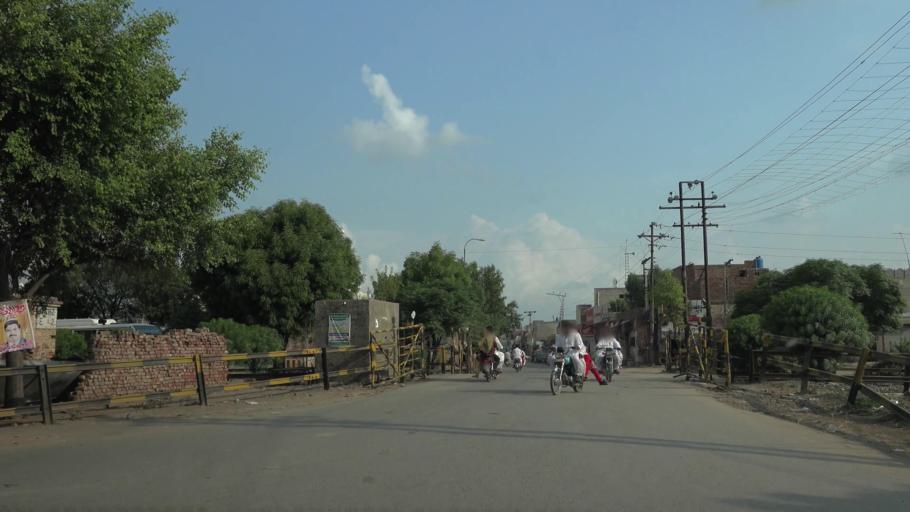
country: PK
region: Punjab
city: Nankana Sahib
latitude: 31.4506
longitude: 73.6980
